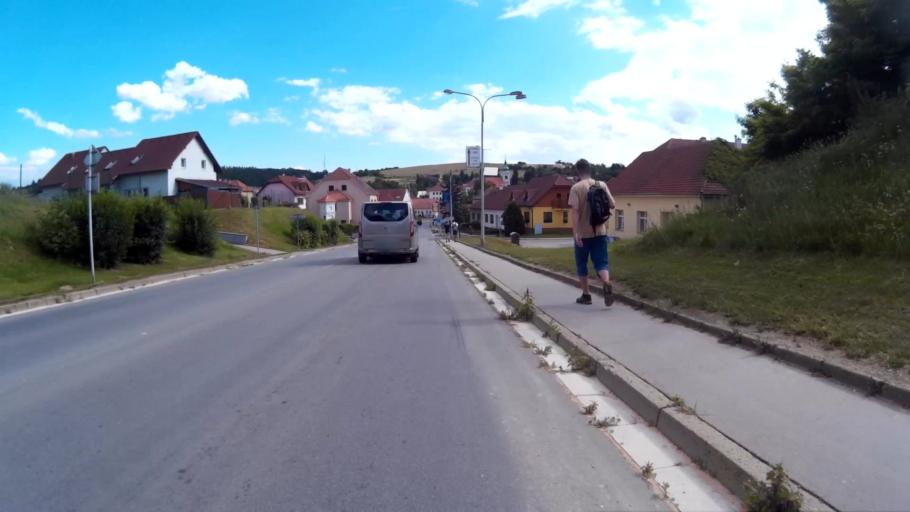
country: CZ
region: South Moravian
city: Strelice
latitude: 49.1544
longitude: 16.5046
